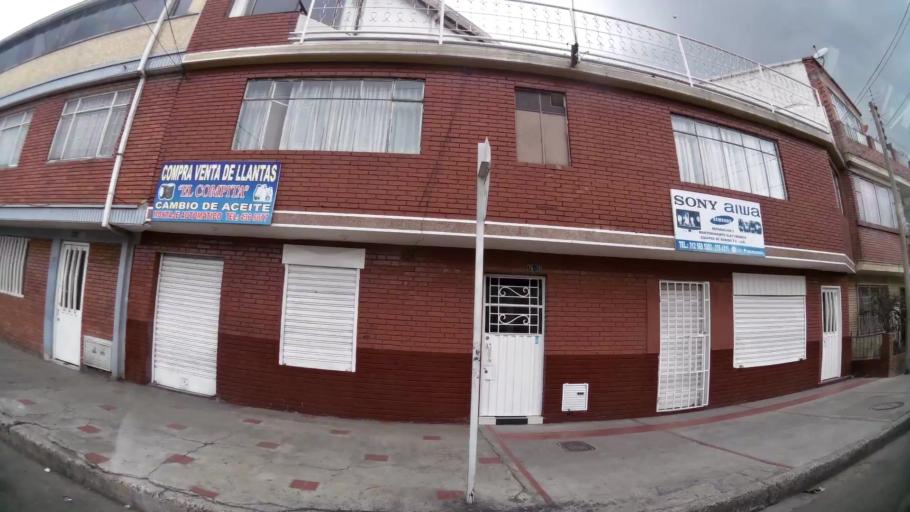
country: CO
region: Bogota D.C.
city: Barrio San Luis
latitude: 4.7067
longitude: -74.0927
